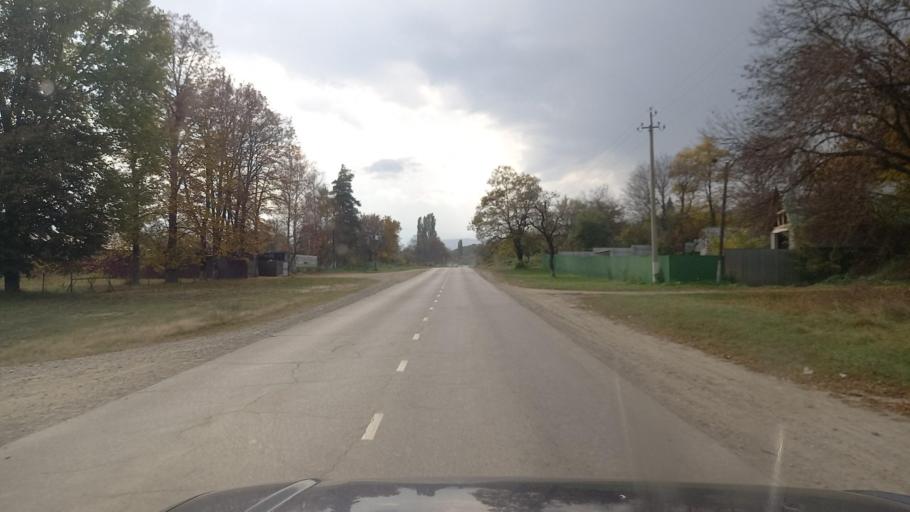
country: RU
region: Krasnodarskiy
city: Psebay
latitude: 44.1351
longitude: 40.8154
